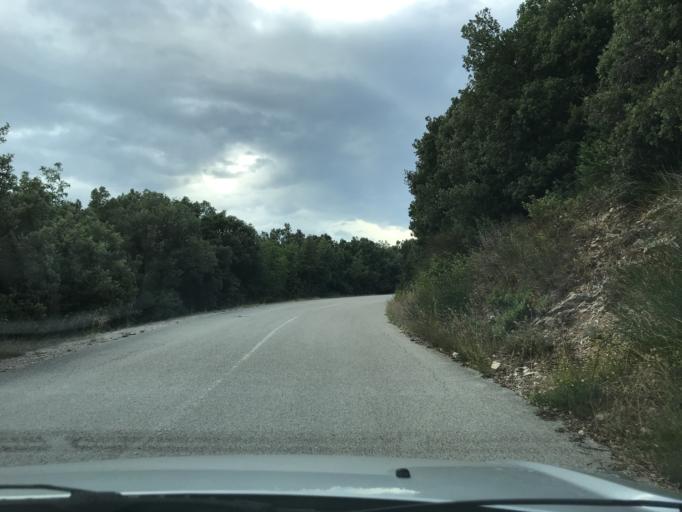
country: IT
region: Umbria
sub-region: Provincia di Terni
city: Montecchio
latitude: 42.6869
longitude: 12.2975
